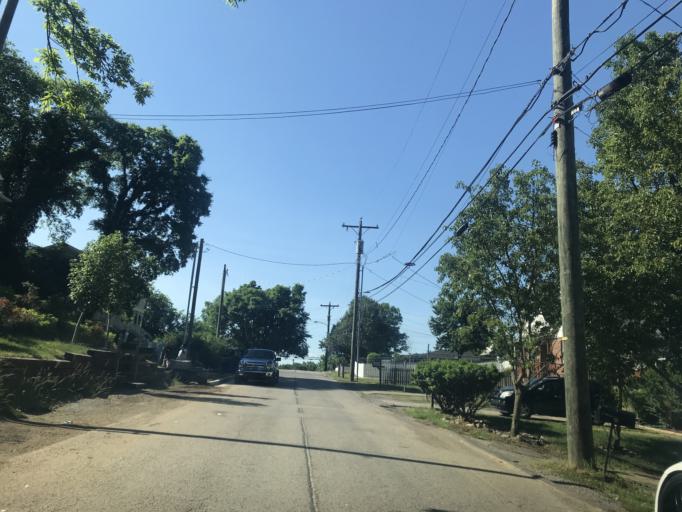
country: US
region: Tennessee
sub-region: Davidson County
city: Nashville
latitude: 36.1870
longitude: -86.8074
